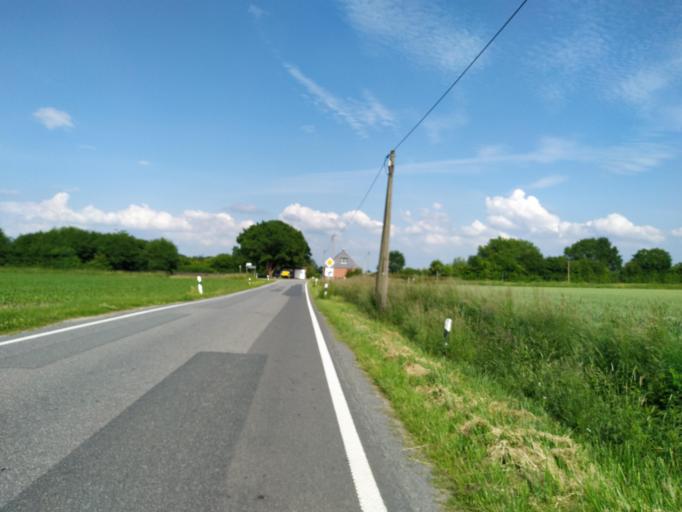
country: DE
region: Schleswig-Holstein
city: Gross Sarau
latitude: 53.7741
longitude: 10.7050
